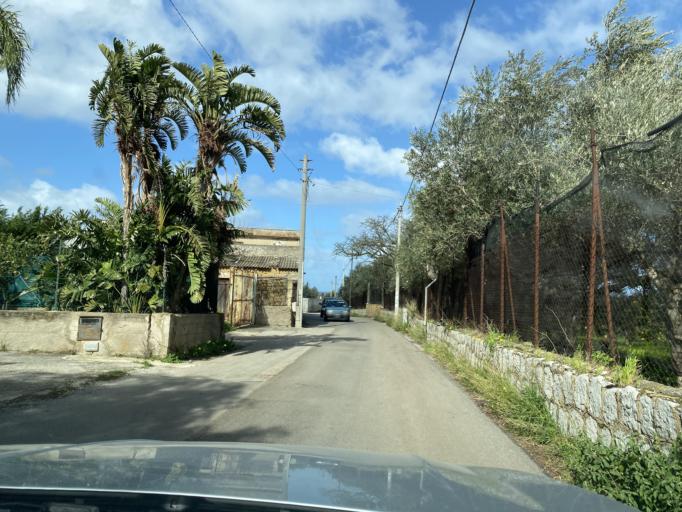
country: IT
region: Sicily
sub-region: Palermo
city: Carini
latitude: 38.1548
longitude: 13.1675
